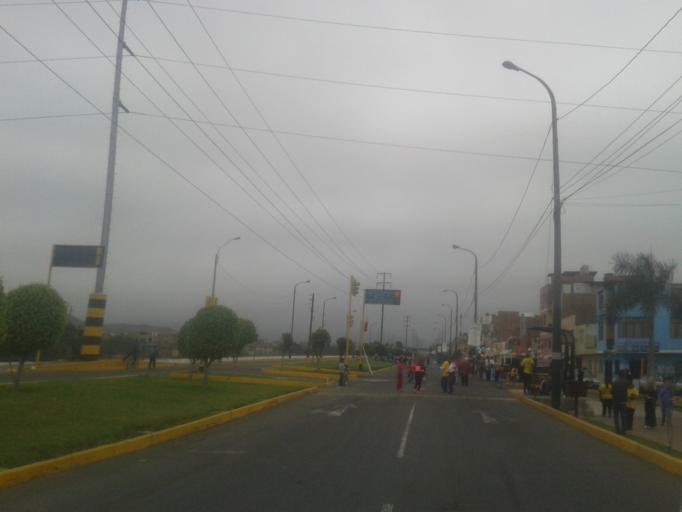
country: PE
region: Callao
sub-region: Callao
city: Callao
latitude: -12.0381
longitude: -77.0887
